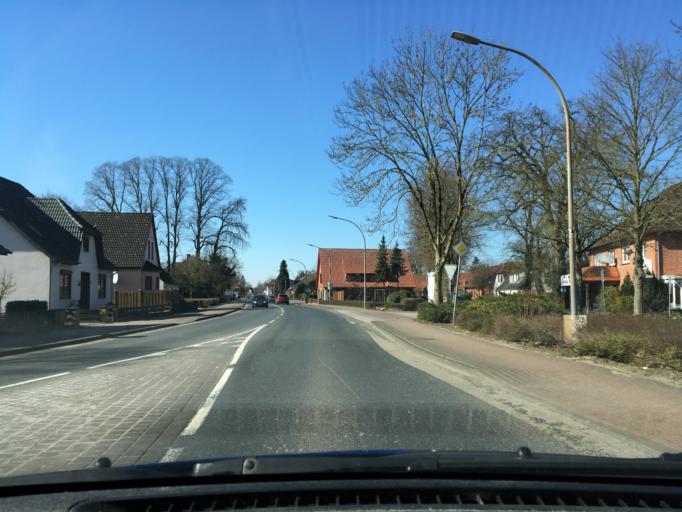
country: DE
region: Lower Saxony
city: Ottersberg
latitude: 53.1079
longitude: 9.1532
